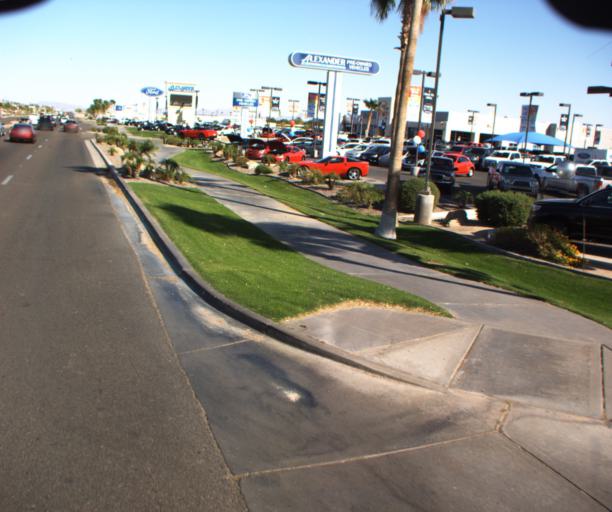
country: US
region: Arizona
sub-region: Yuma County
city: Yuma
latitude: 32.6693
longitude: -114.6124
